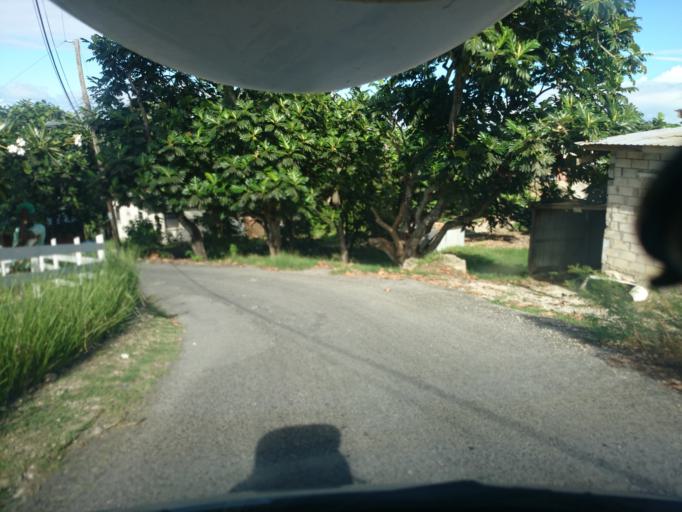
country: BB
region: Saint Joseph
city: Bathsheba
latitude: 13.2119
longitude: -59.5274
